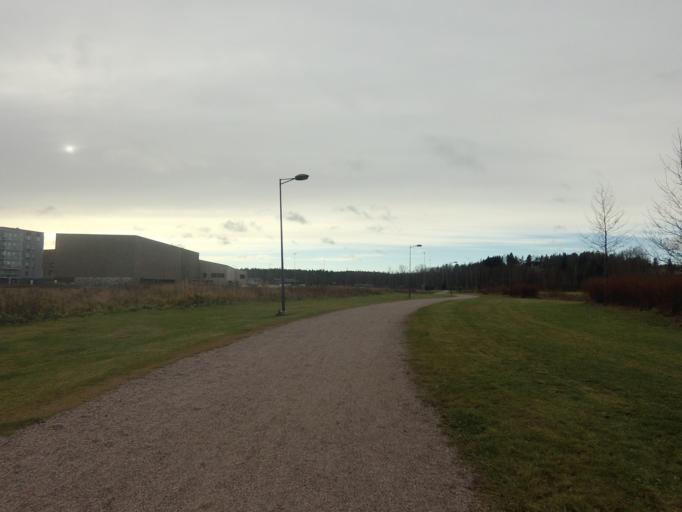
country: FI
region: Uusimaa
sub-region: Helsinki
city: Kauniainen
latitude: 60.1928
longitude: 24.7397
